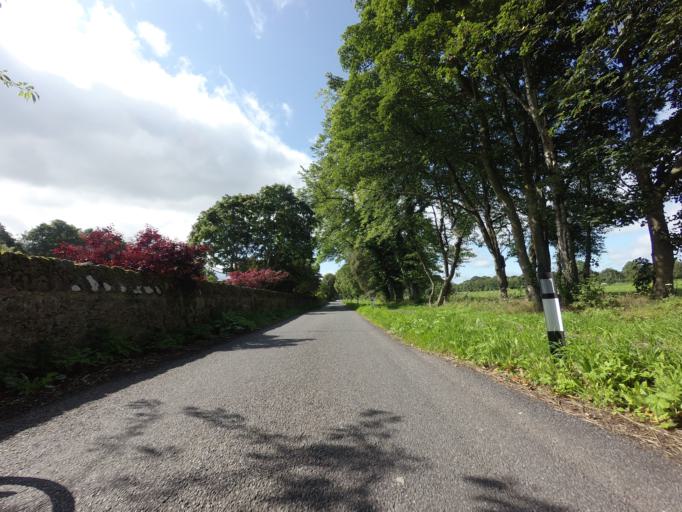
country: GB
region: Scotland
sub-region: Highland
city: Nairn
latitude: 57.5756
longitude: -3.8621
